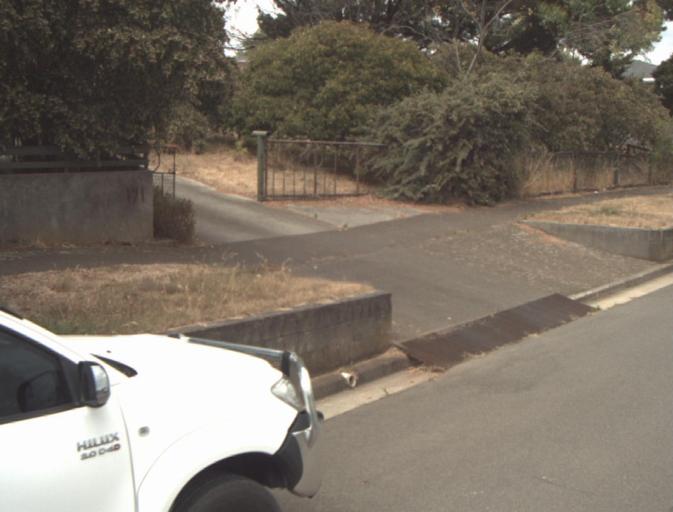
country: AU
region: Tasmania
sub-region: Launceston
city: Newstead
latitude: -41.4488
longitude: 147.1882
